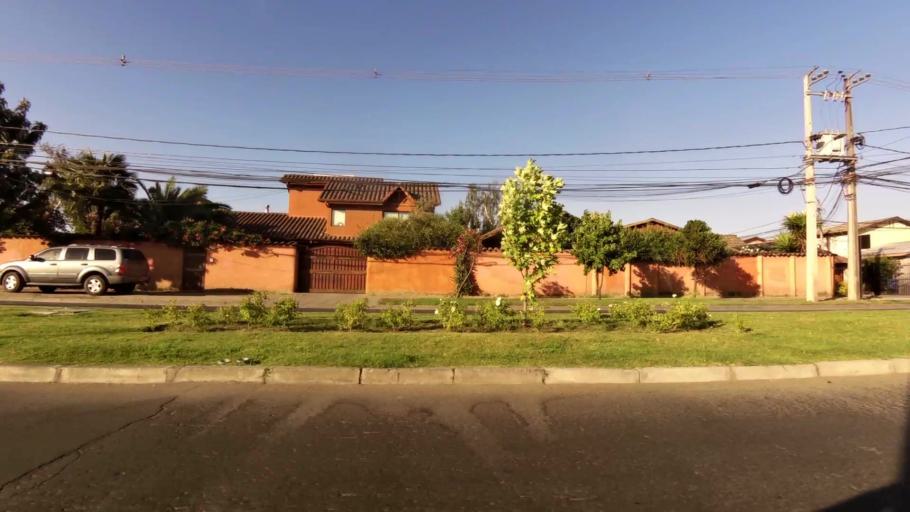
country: CL
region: Maule
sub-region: Provincia de Talca
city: Talca
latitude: -35.4445
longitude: -71.6853
